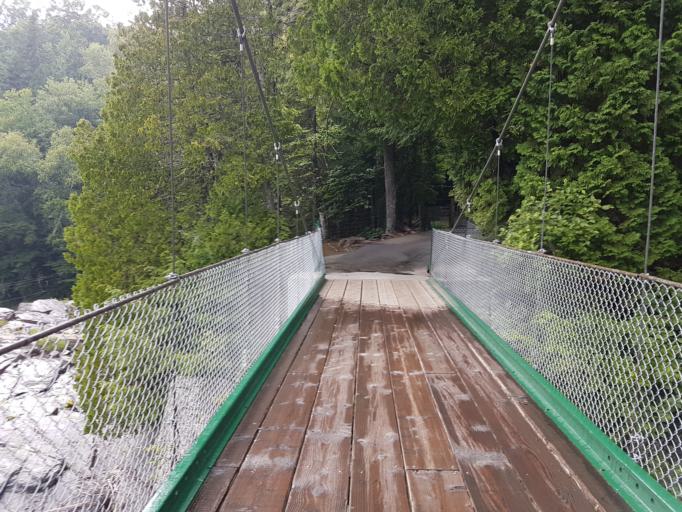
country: CA
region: Quebec
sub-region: Capitale-Nationale
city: Beaupre
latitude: 47.0749
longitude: -70.8757
